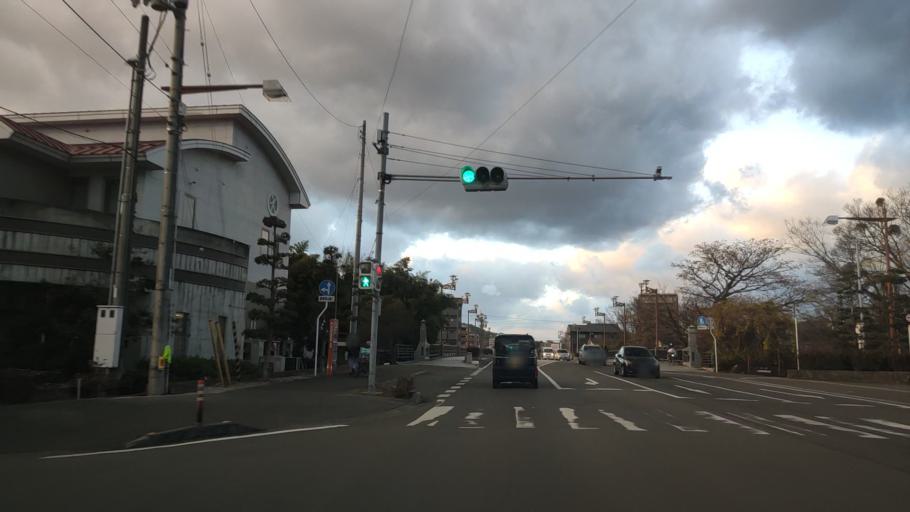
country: JP
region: Ehime
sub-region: Shikoku-chuo Shi
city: Matsuyama
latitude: 33.8388
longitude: 132.7862
